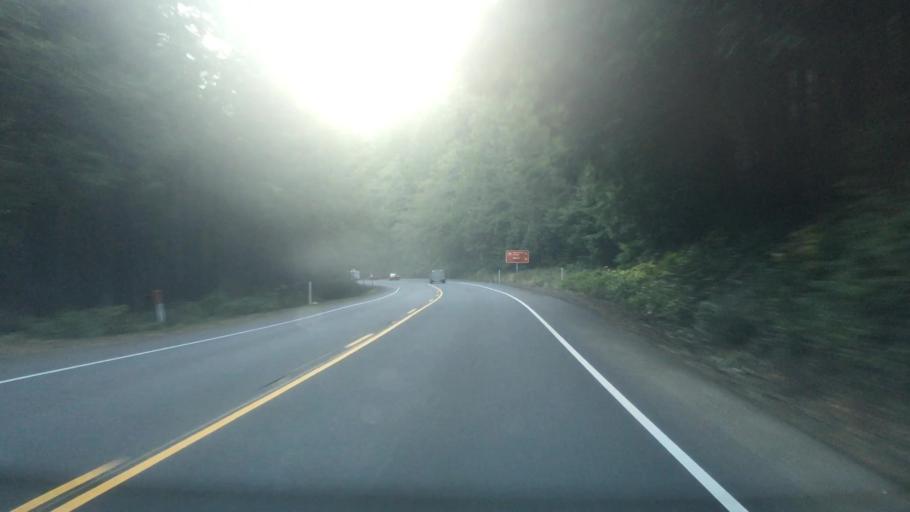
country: US
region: Oregon
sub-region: Clatsop County
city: Cannon Beach
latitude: 45.7694
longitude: -123.9483
